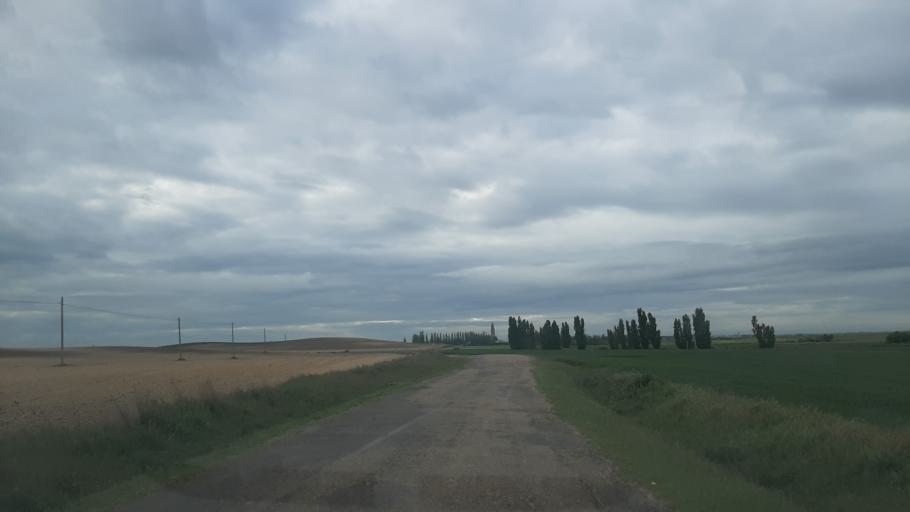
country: ES
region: Castille and Leon
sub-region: Provincia de Salamanca
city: Palaciosrubios
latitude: 41.0644
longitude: -5.2021
